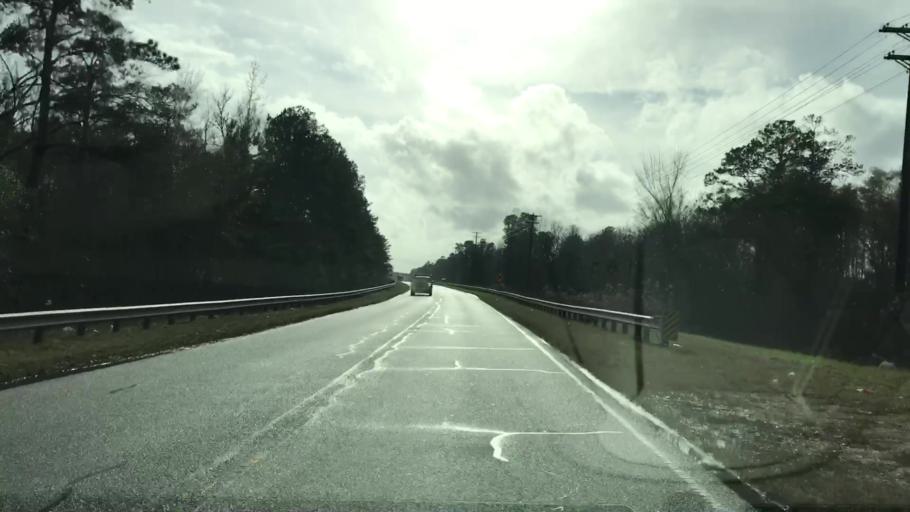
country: US
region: South Carolina
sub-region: Williamsburg County
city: Andrews
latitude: 33.4859
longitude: -79.5508
